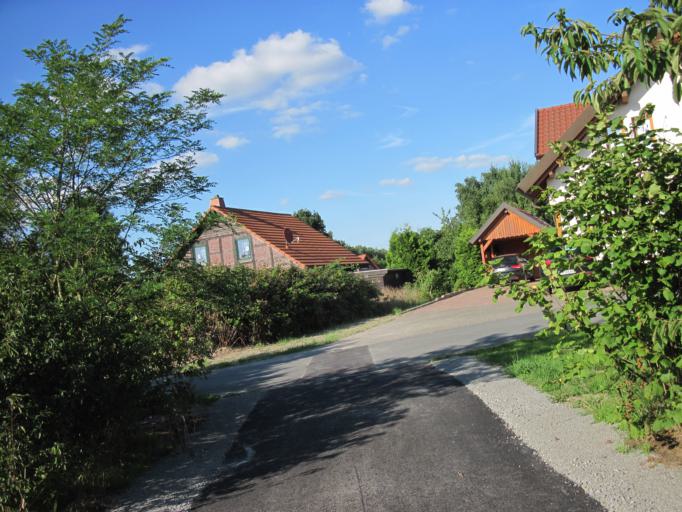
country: DE
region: North Rhine-Westphalia
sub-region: Regierungsbezirk Detmold
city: Delbruck
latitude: 51.7425
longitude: 8.6193
